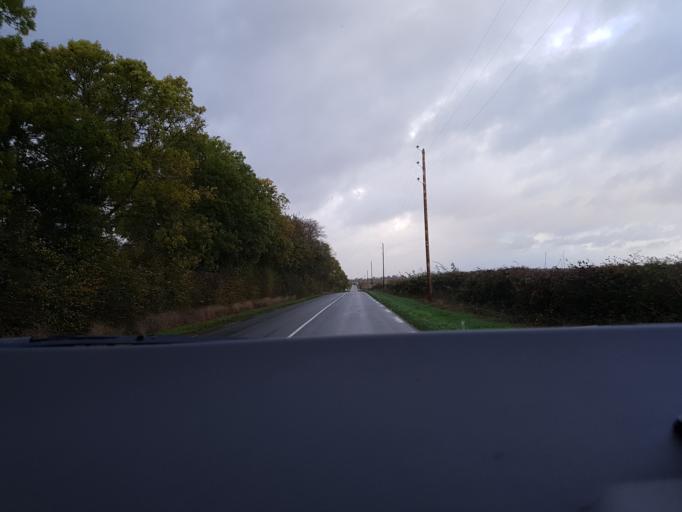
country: FR
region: Poitou-Charentes
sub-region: Departement des Deux-Sevres
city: Brioux-sur-Boutonne
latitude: 46.1687
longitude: -0.1978
